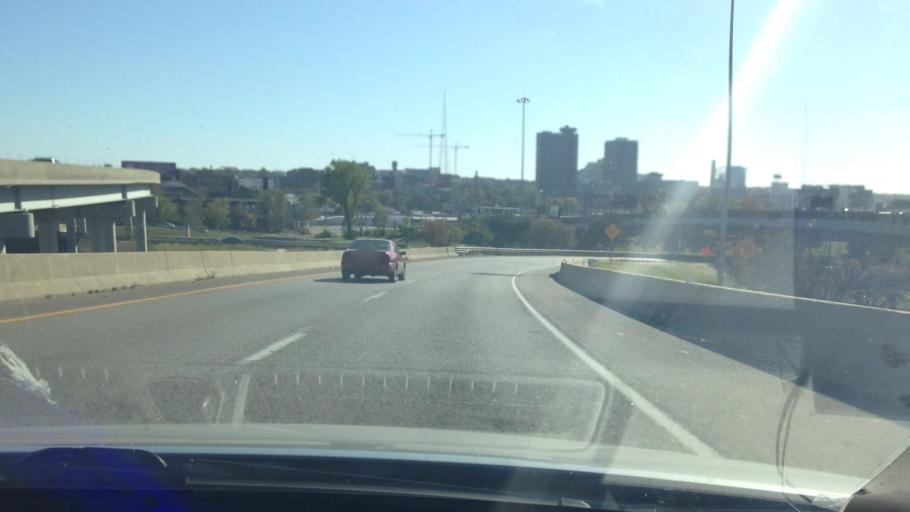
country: US
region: Missouri
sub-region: Jackson County
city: Kansas City
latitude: 39.0970
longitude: -94.5686
